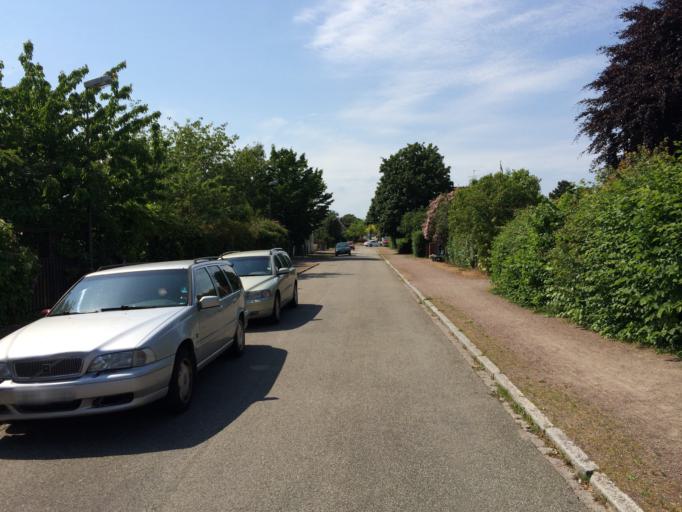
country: SE
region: Skane
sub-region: Malmo
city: Bunkeflostrand
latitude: 55.5765
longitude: 12.9452
